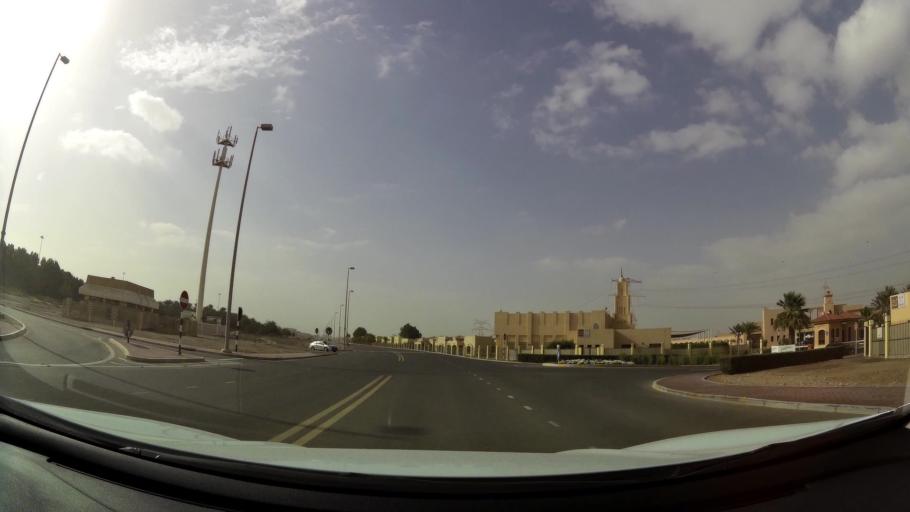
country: AE
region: Abu Dhabi
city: Abu Dhabi
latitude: 24.4064
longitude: 54.5258
